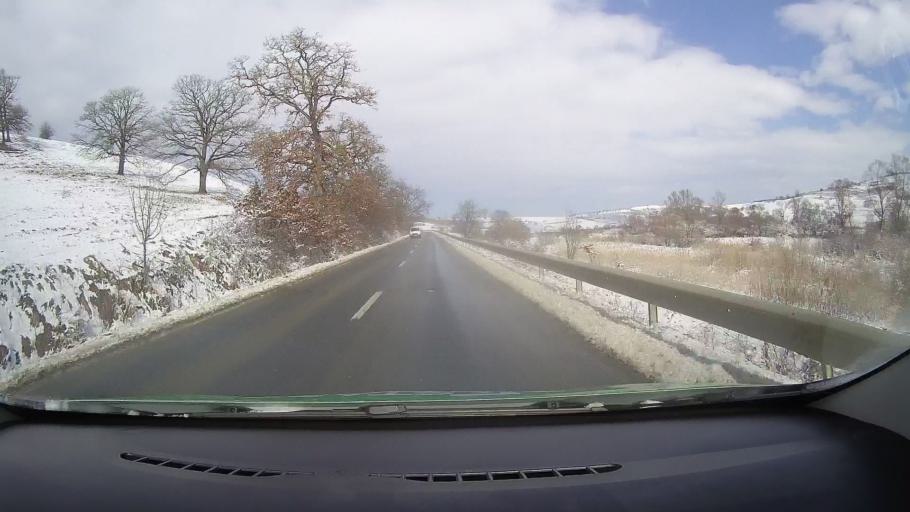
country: RO
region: Sibiu
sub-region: Comuna Altina
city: Altina
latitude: 45.9528
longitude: 24.4530
